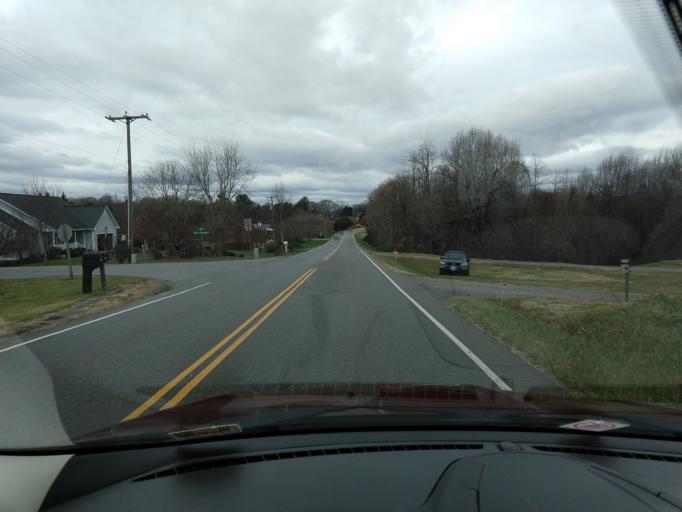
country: US
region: Virginia
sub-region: Botetourt County
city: Blue Ridge
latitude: 37.2557
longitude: -79.7200
